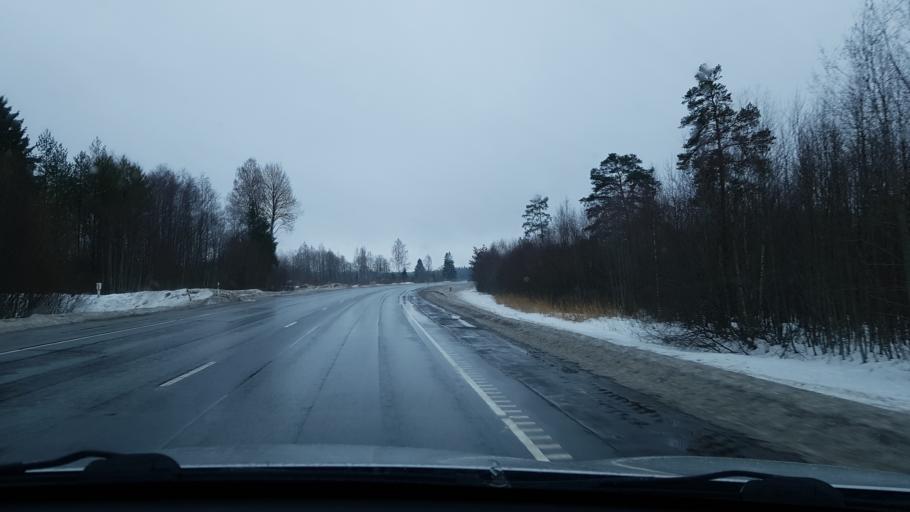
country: EE
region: Raplamaa
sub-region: Kohila vald
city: Kohila
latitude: 59.1931
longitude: 24.7873
